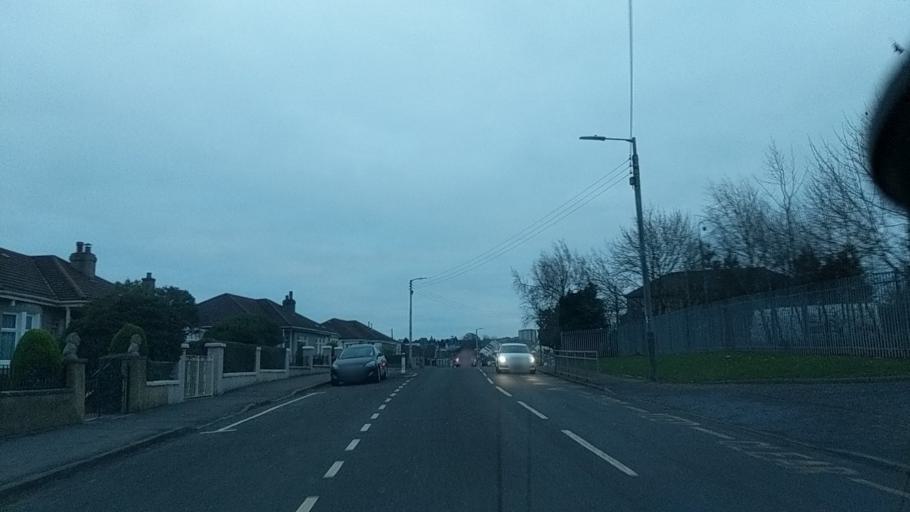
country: GB
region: Scotland
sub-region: South Lanarkshire
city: Rutherglen
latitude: 55.8210
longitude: -4.1950
